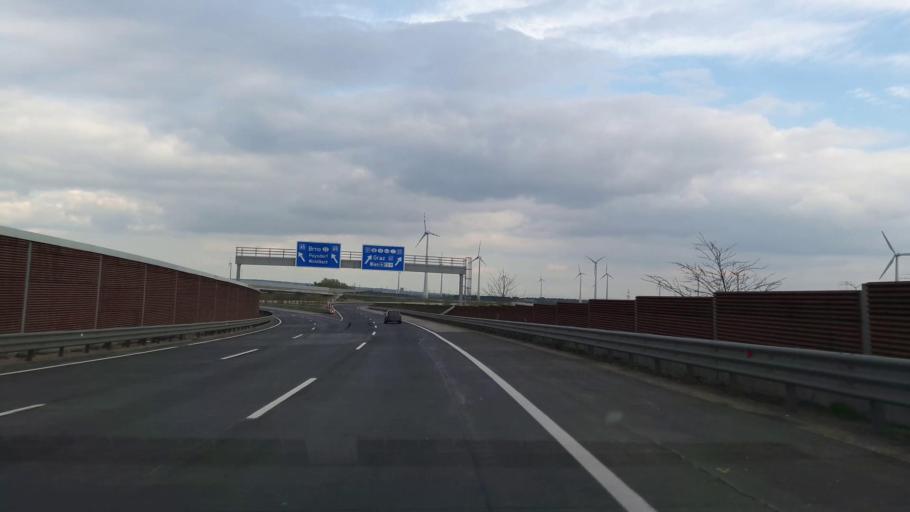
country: AT
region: Lower Austria
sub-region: Politischer Bezirk Mistelbach
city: Grossebersdorf
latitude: 48.3471
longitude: 16.4771
